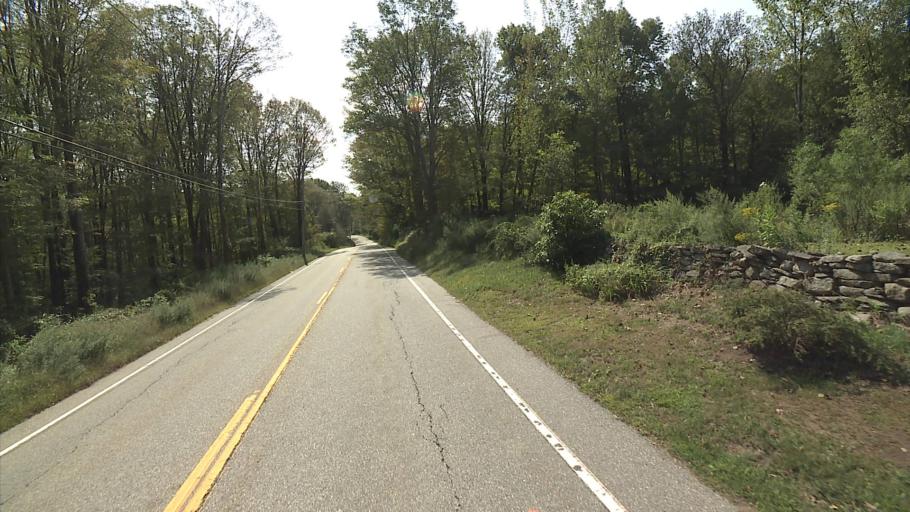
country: US
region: Connecticut
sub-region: Windham County
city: East Brooklyn
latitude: 41.8114
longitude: -71.9554
